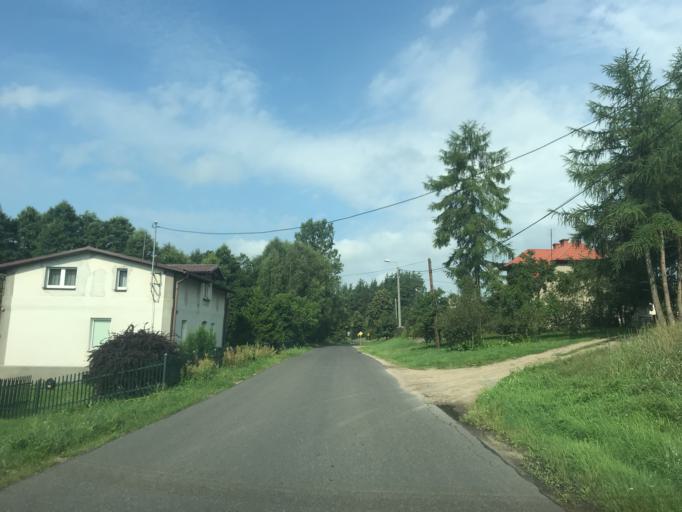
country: PL
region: Warmian-Masurian Voivodeship
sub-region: Powiat nowomiejski
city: Kurzetnik
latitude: 53.3704
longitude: 19.5424
